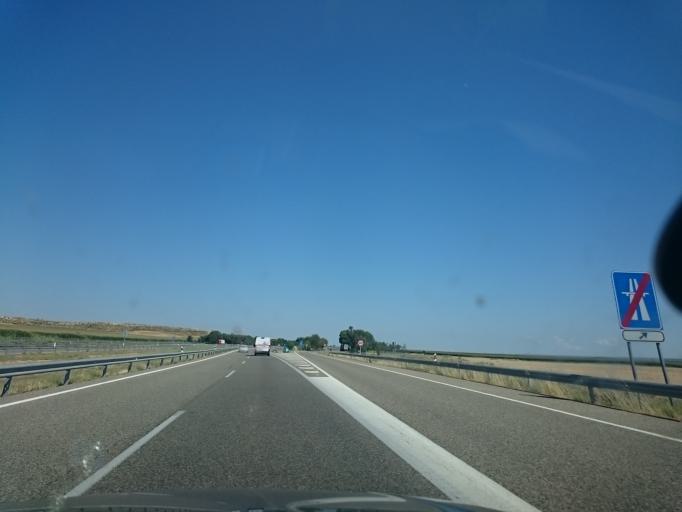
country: ES
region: Aragon
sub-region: Provincia de Huesca
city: Candasnos
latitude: 41.5095
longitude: 0.0907
